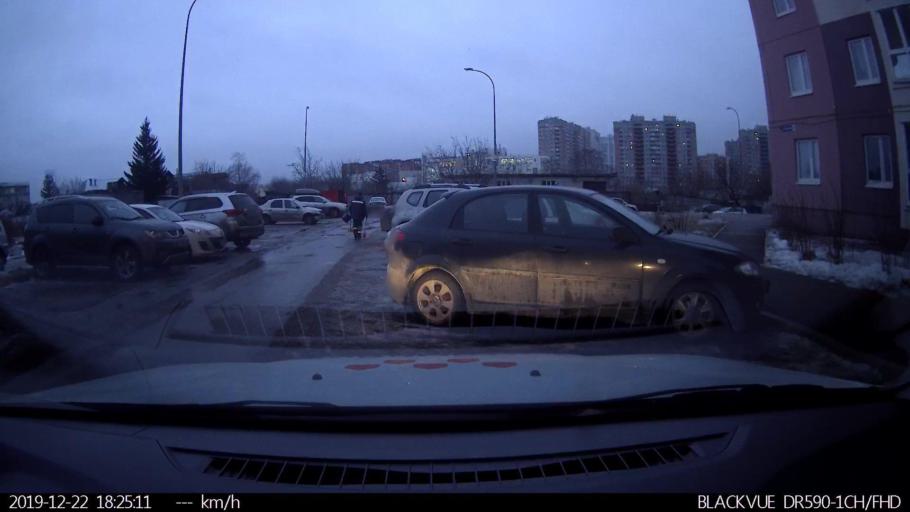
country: RU
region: Nizjnij Novgorod
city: Bor
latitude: 56.3162
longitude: 44.0638
